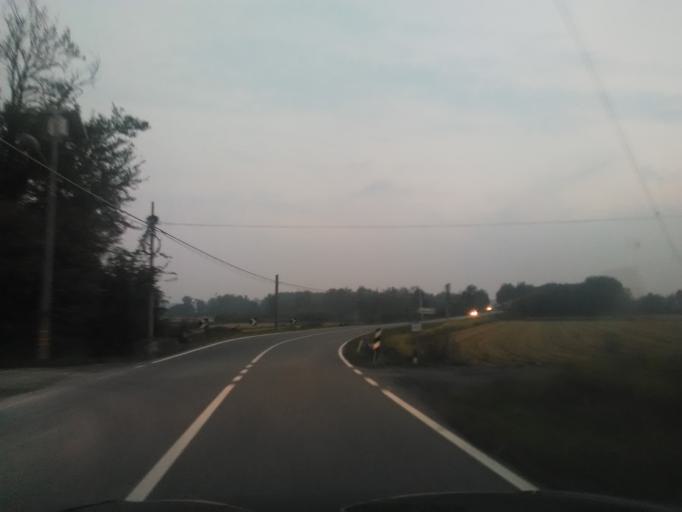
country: IT
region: Piedmont
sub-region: Provincia di Vercelli
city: Carisio
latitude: 45.4222
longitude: 8.2111
